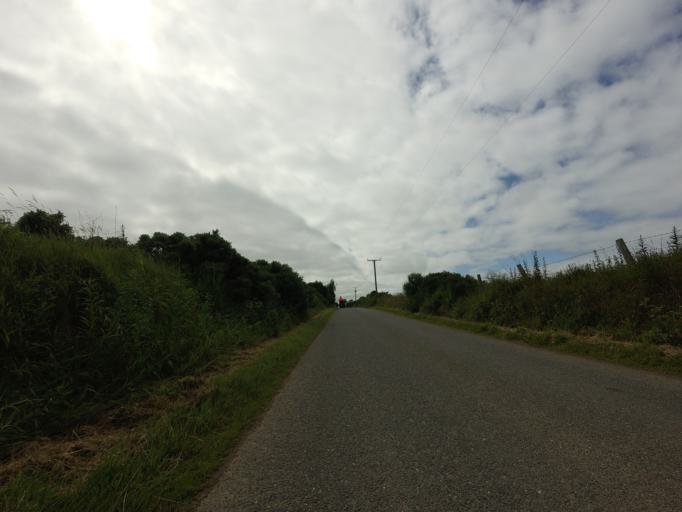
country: GB
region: Scotland
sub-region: Aberdeenshire
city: Turriff
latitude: 57.5450
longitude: -2.2832
